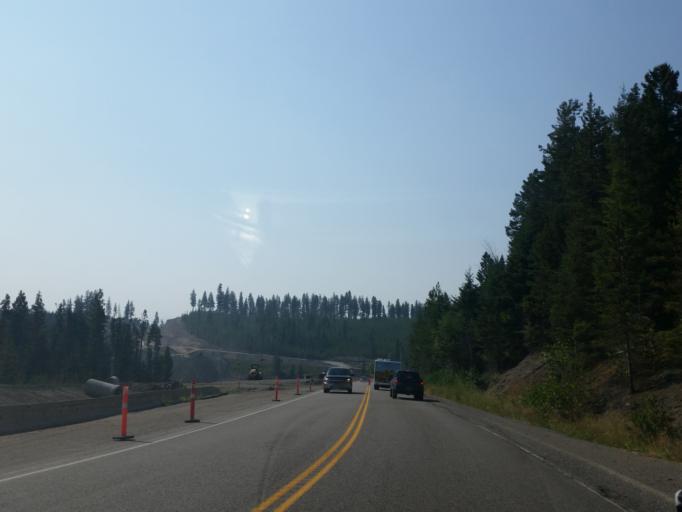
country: CA
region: British Columbia
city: Princeton
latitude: 49.2823
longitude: -120.5807
